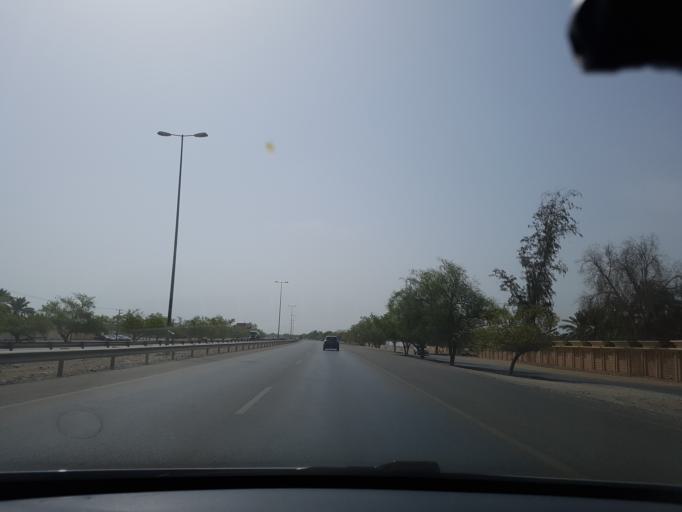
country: OM
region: Al Batinah
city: Al Khaburah
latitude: 23.9470
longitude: 57.1126
